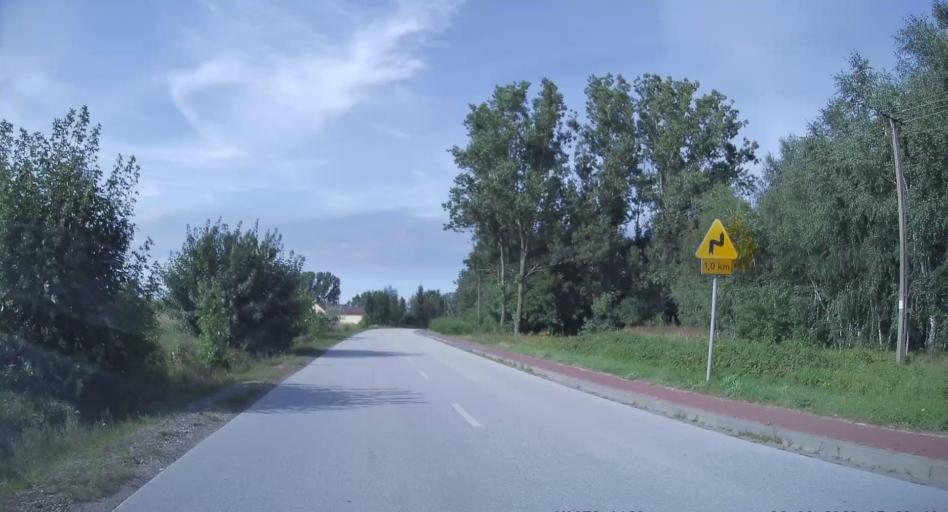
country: PL
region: Lodz Voivodeship
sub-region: Powiat opoczynski
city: Mniszkow
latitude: 51.3472
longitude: 20.0380
